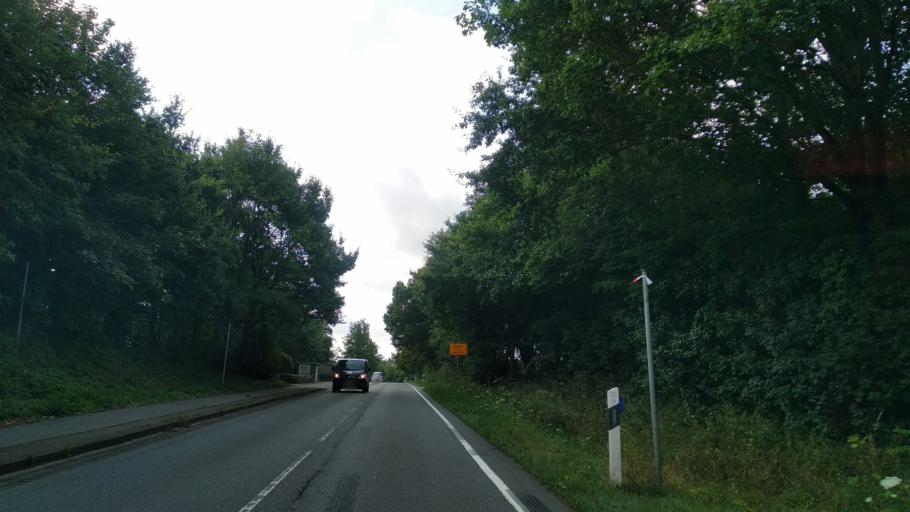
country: DE
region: Schleswig-Holstein
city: Selk
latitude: 54.4748
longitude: 9.5656
